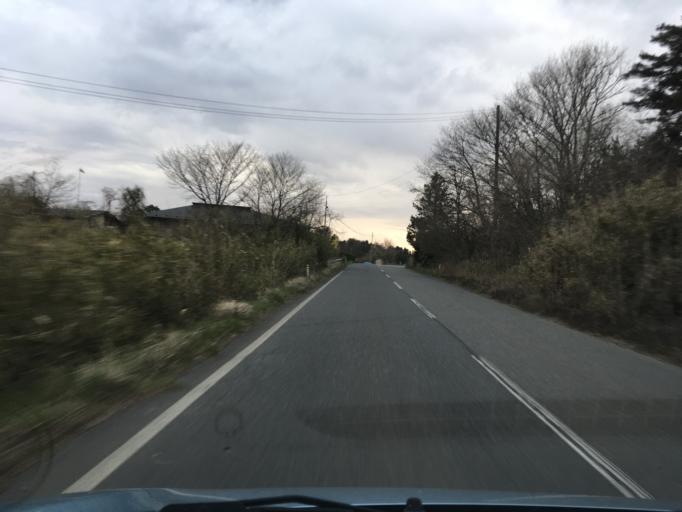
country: JP
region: Iwate
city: Ichinoseki
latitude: 38.7779
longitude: 141.2443
